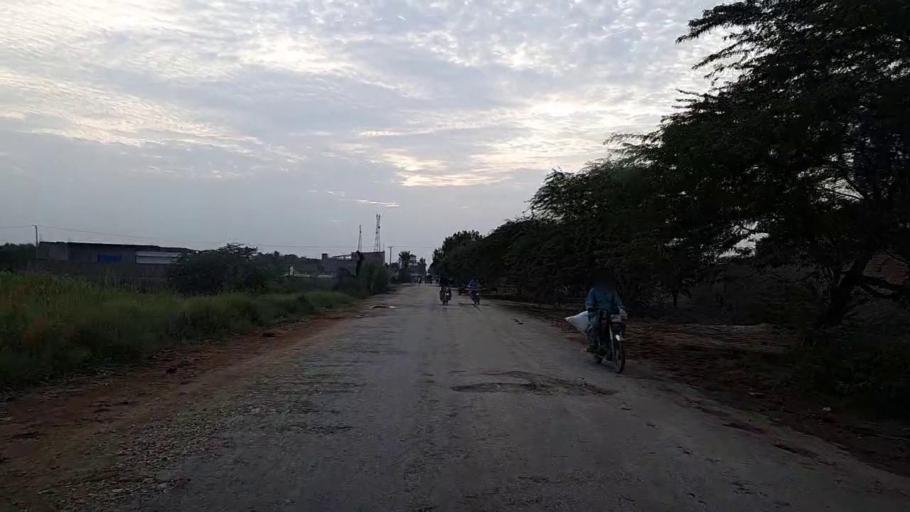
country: PK
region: Sindh
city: Naushahro Firoz
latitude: 26.8088
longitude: 68.2023
